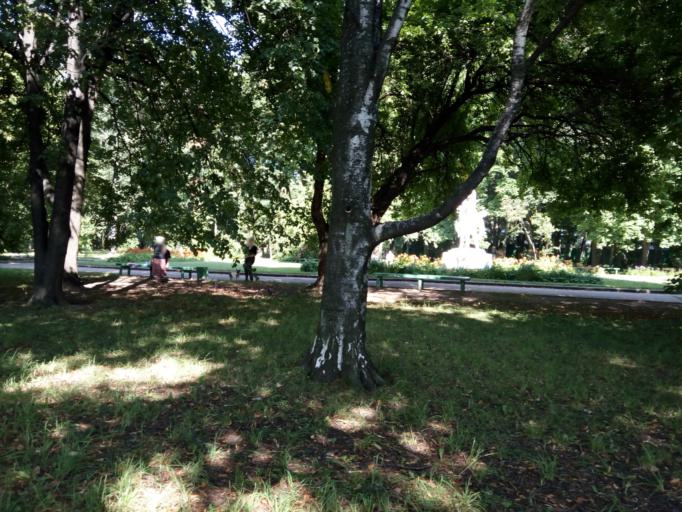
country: RU
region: Moskovskaya
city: Levoberezhnyy
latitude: 55.8529
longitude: 37.4660
